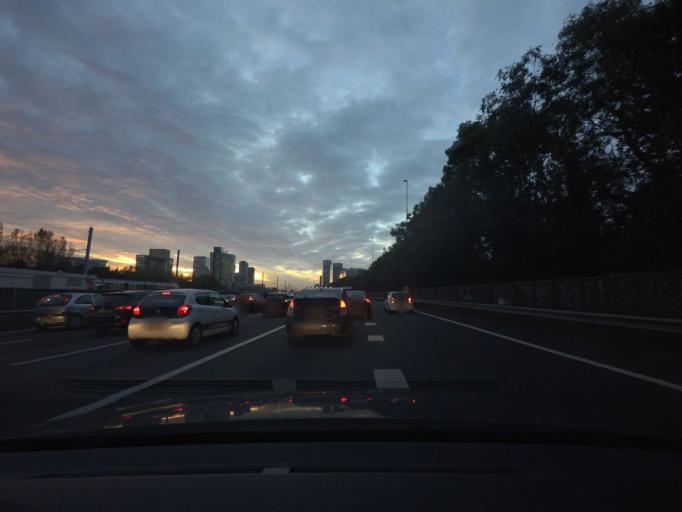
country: NL
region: North Holland
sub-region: Gemeente Amsterdam
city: Amsterdam
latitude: 52.3397
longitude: 4.8843
